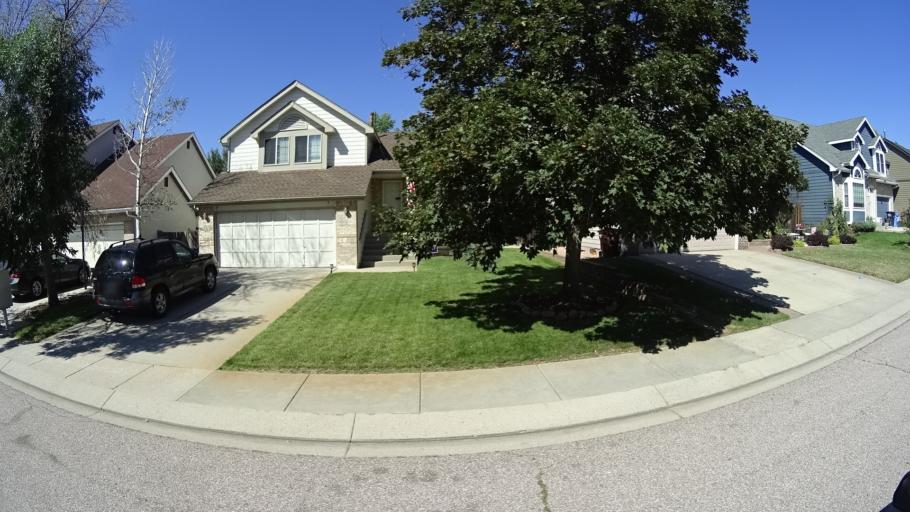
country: US
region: Colorado
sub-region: El Paso County
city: Black Forest
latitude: 38.9578
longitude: -104.7516
